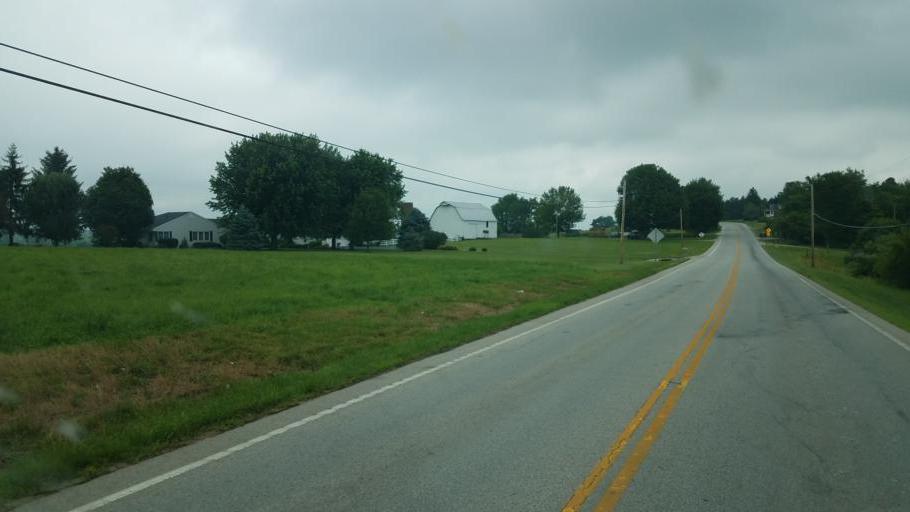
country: US
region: Ohio
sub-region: Highland County
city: Hillsboro
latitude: 39.2056
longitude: -83.5793
